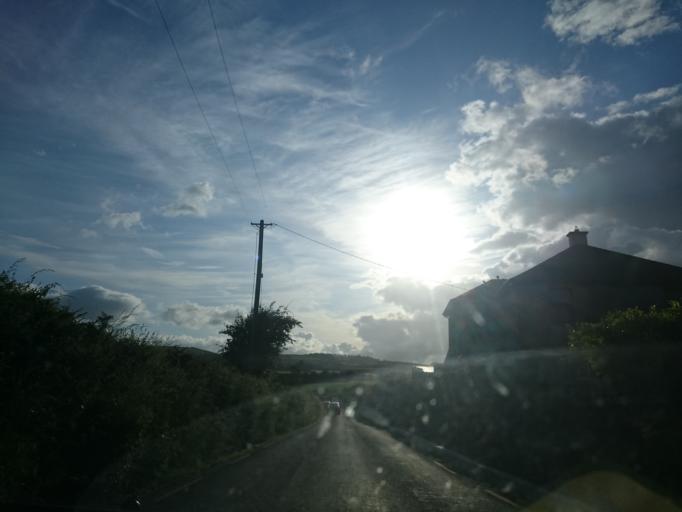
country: IE
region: Leinster
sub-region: Loch Garman
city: New Ross
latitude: 52.4093
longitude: -7.0036
